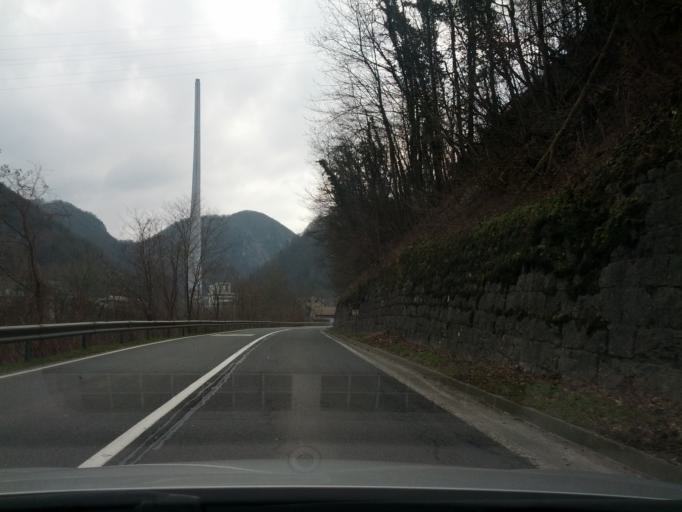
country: SI
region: Trbovlje
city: Trbovlje
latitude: 46.1261
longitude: 15.0488
